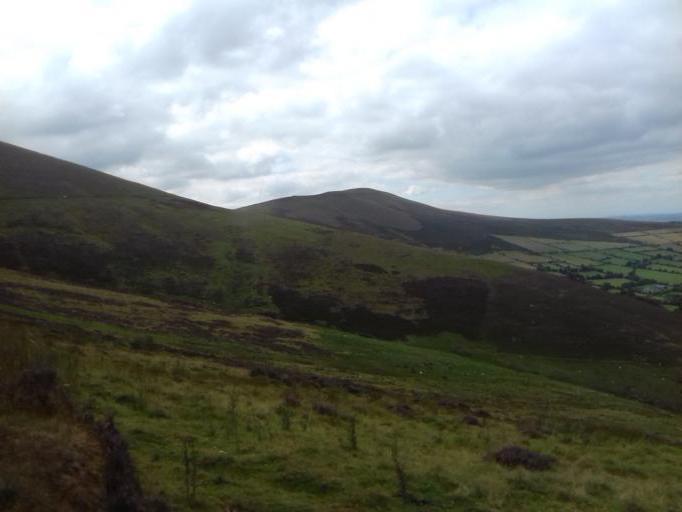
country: IE
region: Leinster
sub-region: Loch Garman
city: Bunclody
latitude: 52.6422
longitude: -6.7738
